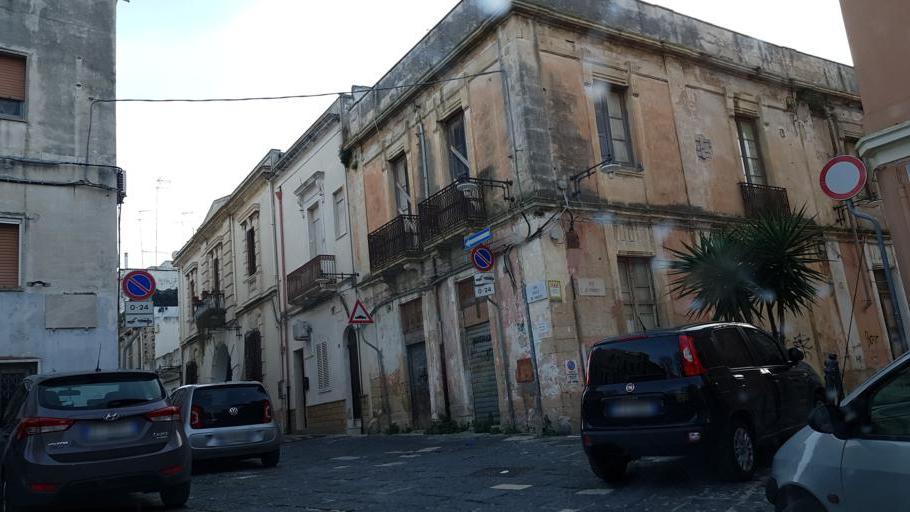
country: IT
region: Apulia
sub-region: Provincia di Brindisi
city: Brindisi
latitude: 40.6365
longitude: 17.9469
